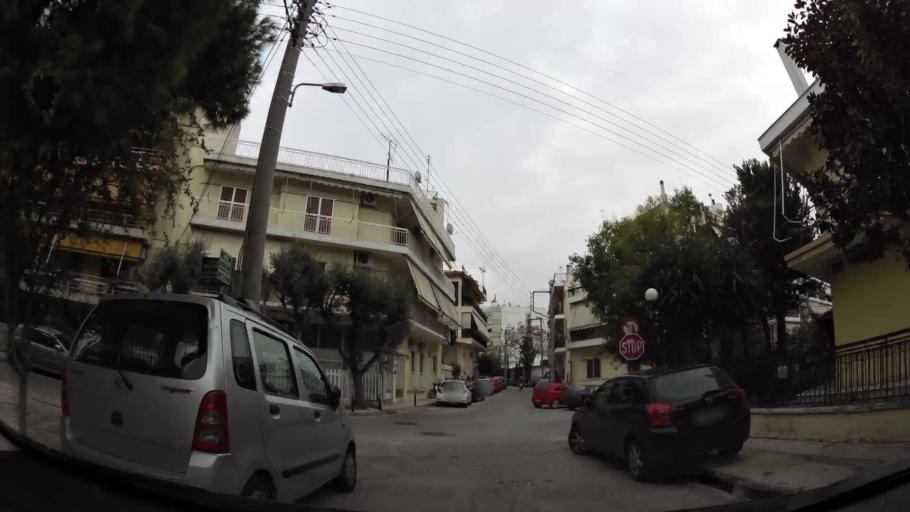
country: GR
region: Attica
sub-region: Nomarchia Athinas
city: Nea Ionia
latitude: 38.0397
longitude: 23.7698
